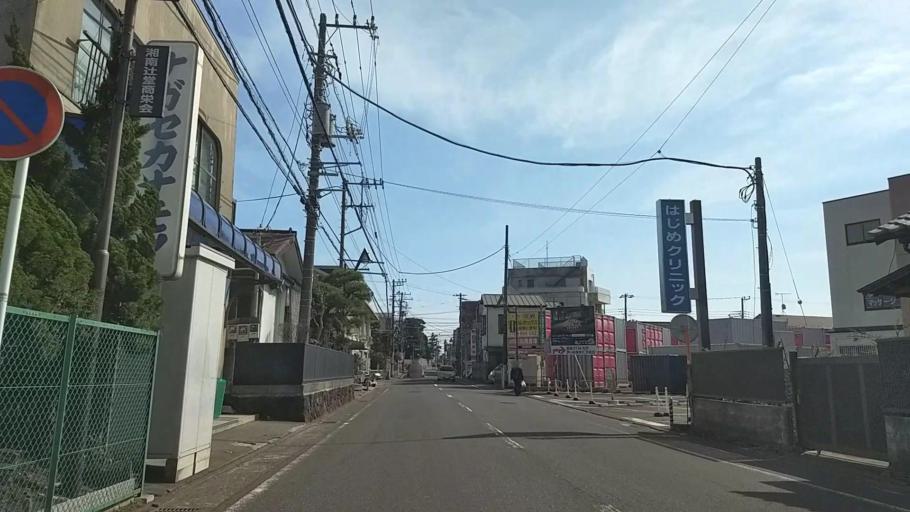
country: JP
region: Kanagawa
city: Fujisawa
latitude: 35.3286
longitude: 139.4524
